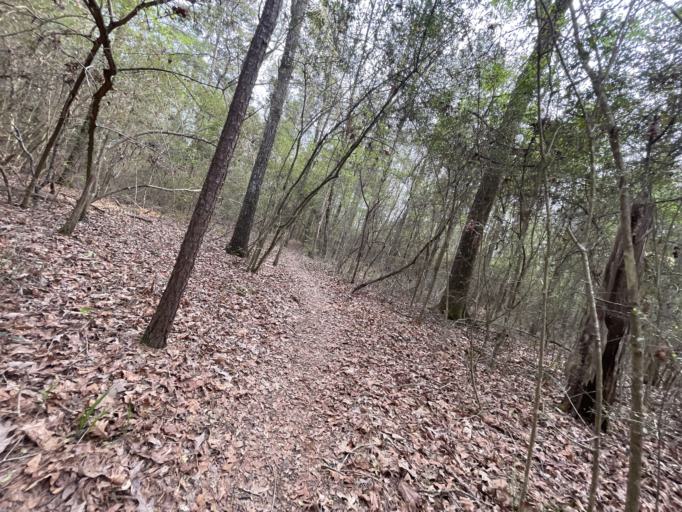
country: US
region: Texas
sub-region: Walker County
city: Huntsville
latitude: 30.6612
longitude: -95.4866
